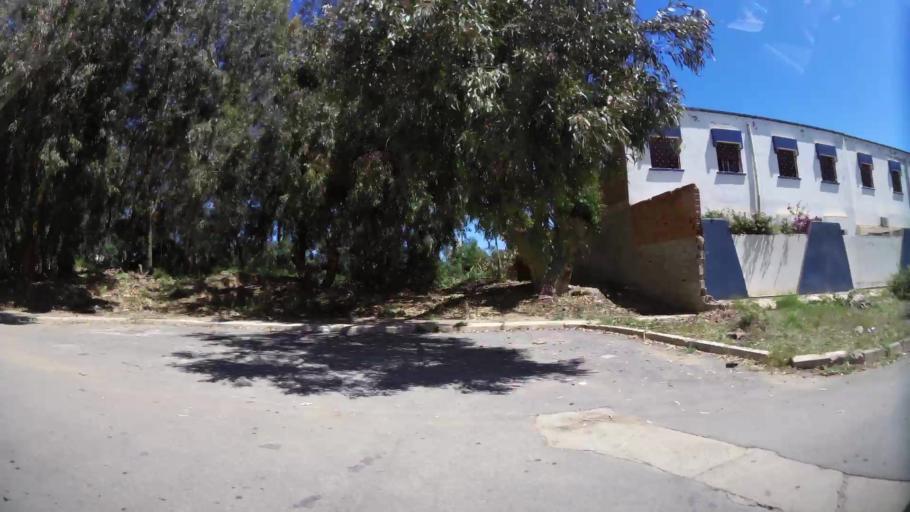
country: MA
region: Oriental
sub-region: Berkane-Taourirt
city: Madagh
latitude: 35.0869
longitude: -2.2386
